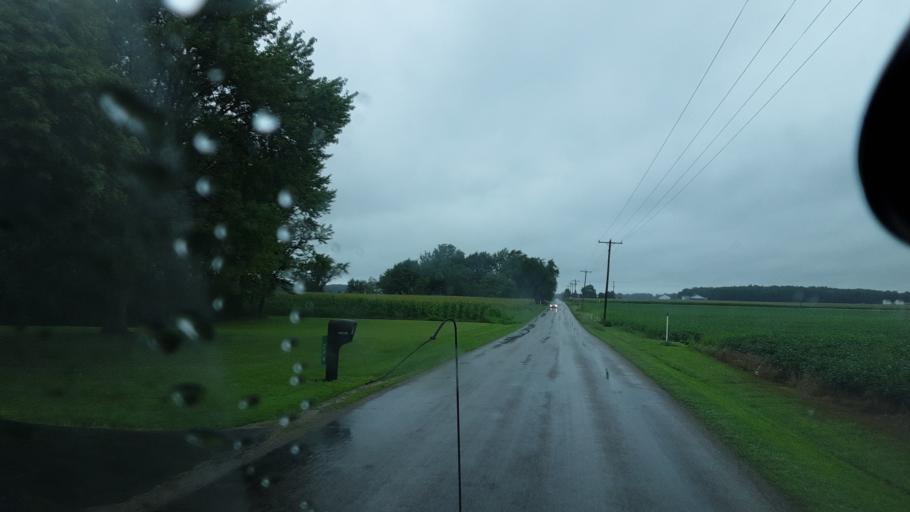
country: US
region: Indiana
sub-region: Adams County
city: Decatur
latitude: 40.7427
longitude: -84.8556
